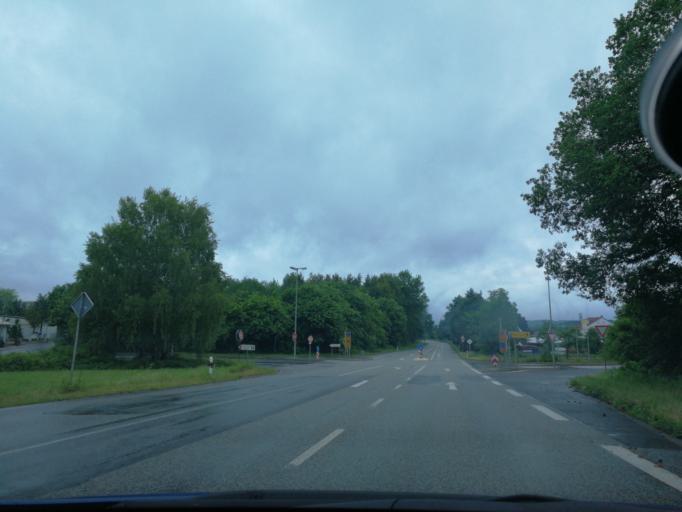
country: DE
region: Rheinland-Pfalz
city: Mehlingen
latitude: 49.4915
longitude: 7.8484
